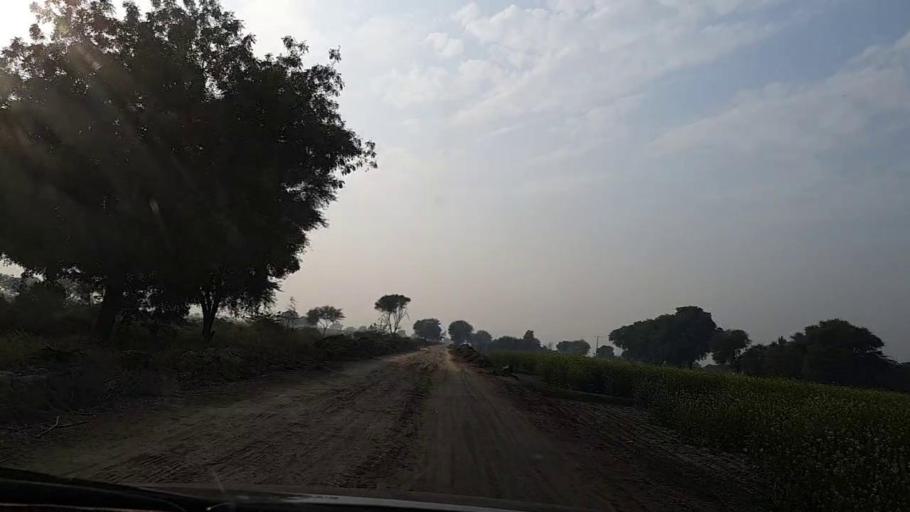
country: PK
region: Sindh
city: Nawabshah
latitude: 26.2695
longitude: 68.3232
